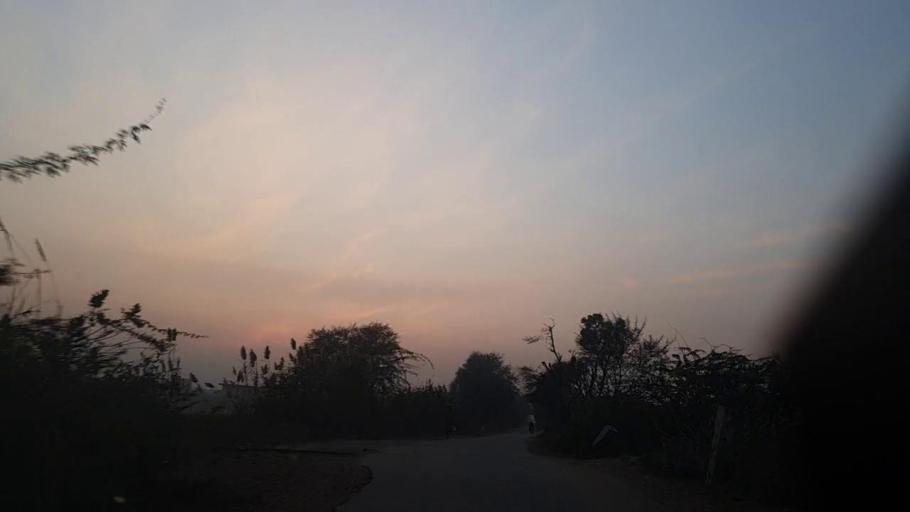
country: PK
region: Sindh
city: Sakrand
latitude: 26.1021
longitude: 68.3074
